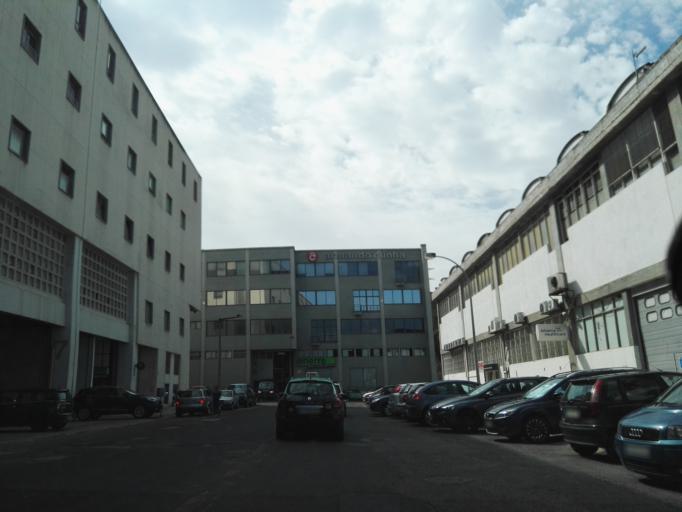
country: PT
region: Lisbon
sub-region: Loures
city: Moscavide
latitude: 38.7476
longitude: -9.0984
